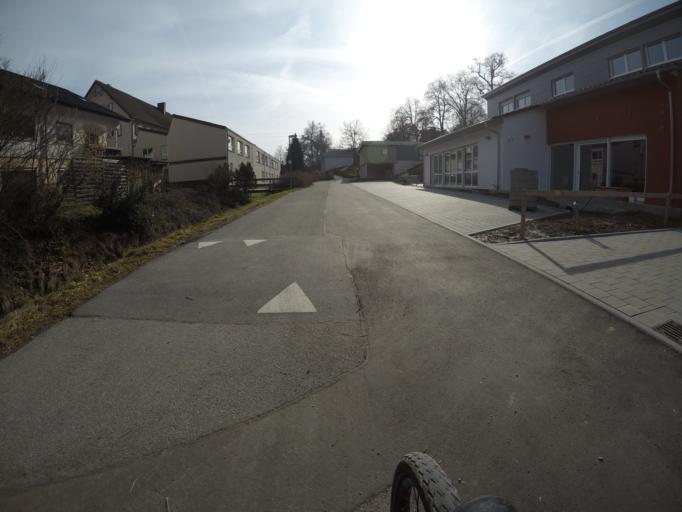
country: DE
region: Baden-Wuerttemberg
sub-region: Karlsruhe Region
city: Wildberg
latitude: 48.6180
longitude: 8.7788
